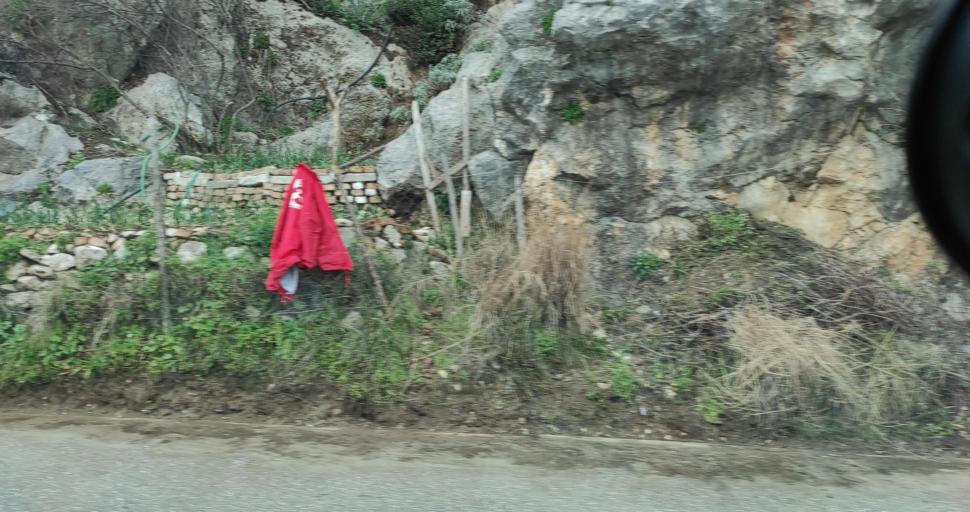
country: AL
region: Lezhe
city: Shengjin
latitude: 41.8073
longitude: 19.6072
